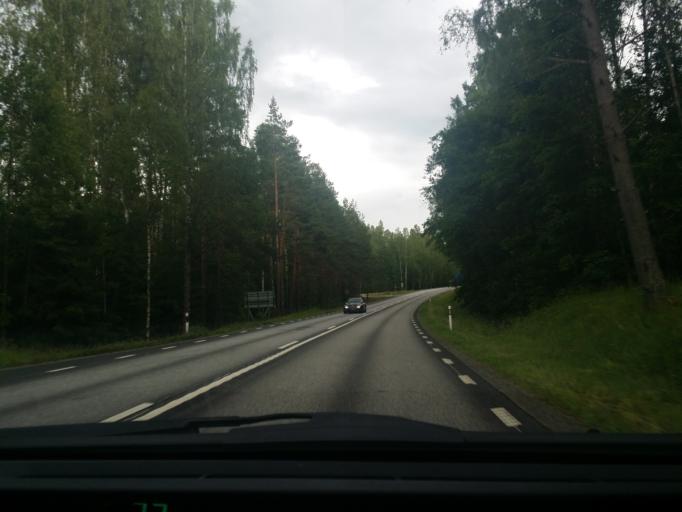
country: SE
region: OErebro
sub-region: Nora Kommun
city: Nora
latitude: 59.4745
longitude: 15.1235
